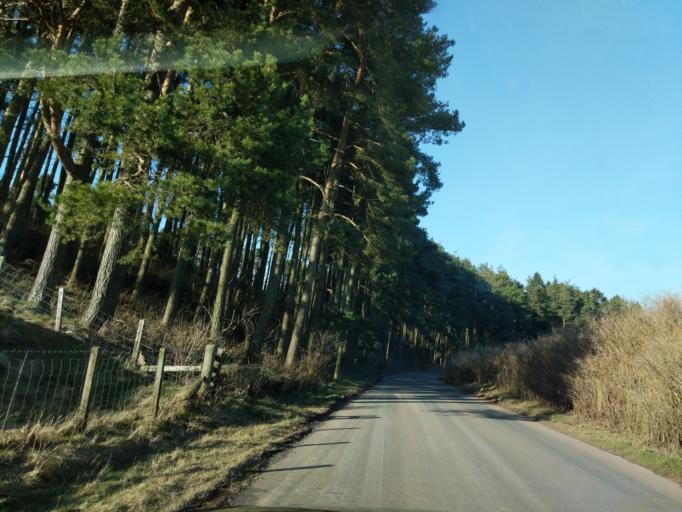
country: GB
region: Scotland
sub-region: The Scottish Borders
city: West Linton
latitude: 55.7197
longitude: -3.4354
